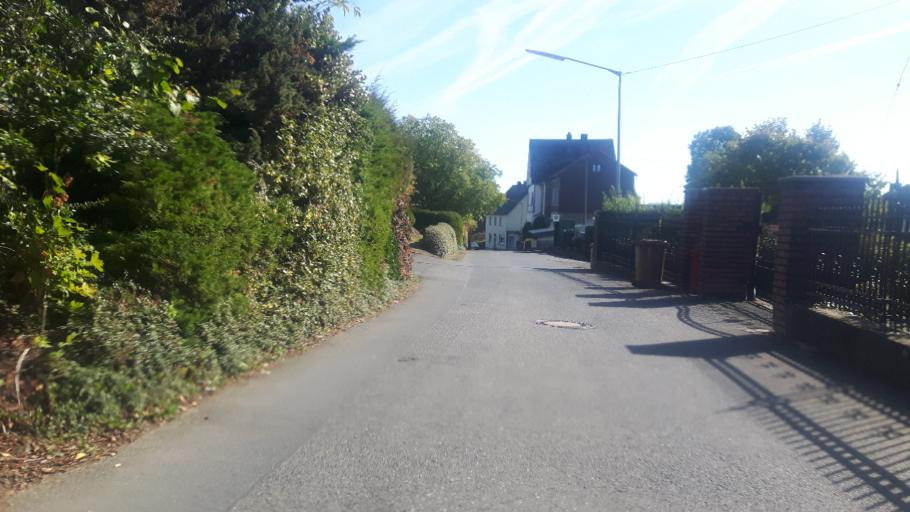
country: DE
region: Rheinland-Pfalz
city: Etzbach
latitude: 50.7870
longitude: 7.6939
